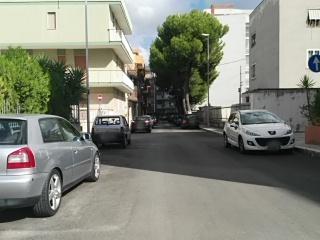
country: IT
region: Apulia
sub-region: Provincia di Bari
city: Triggiano
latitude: 41.0618
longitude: 16.9139
